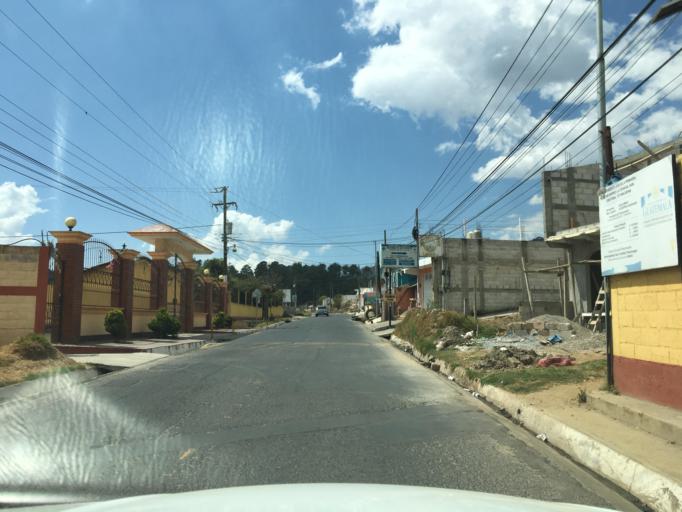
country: GT
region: Quetzaltenango
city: Salcaja
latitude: 14.9063
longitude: -91.4559
